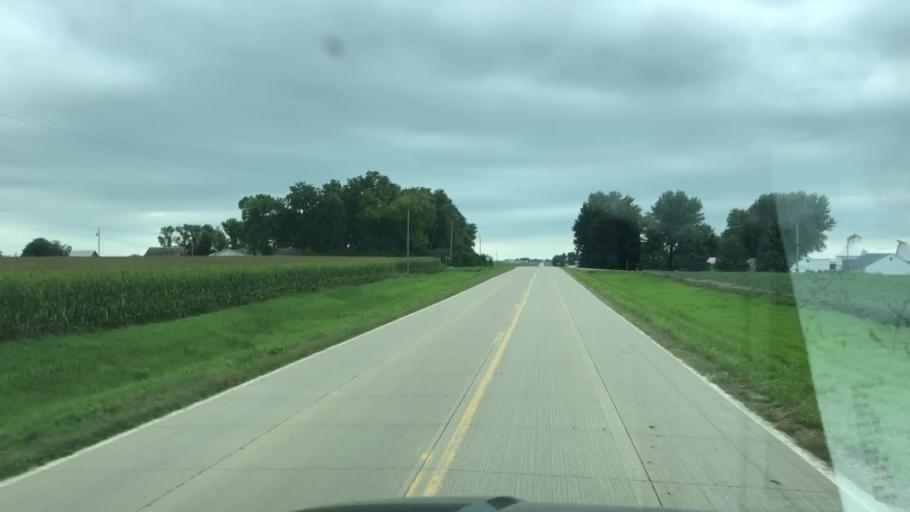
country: US
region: Iowa
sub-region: O'Brien County
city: Sheldon
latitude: 43.1436
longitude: -95.9795
